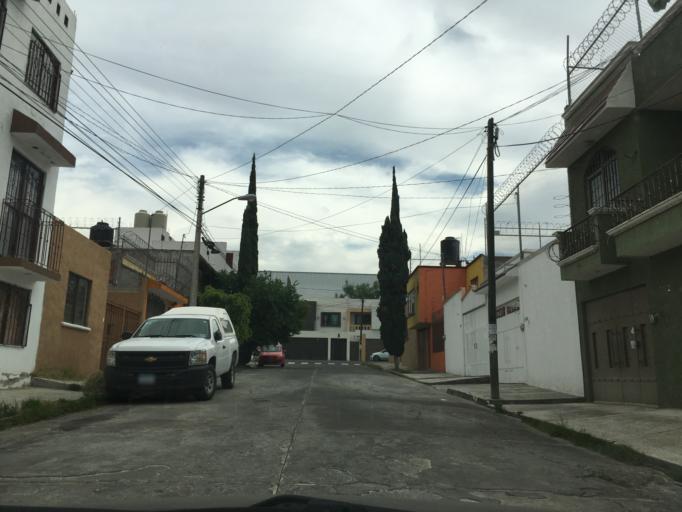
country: MX
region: Michoacan
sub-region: Morelia
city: Morelos
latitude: 19.6702
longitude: -101.2122
